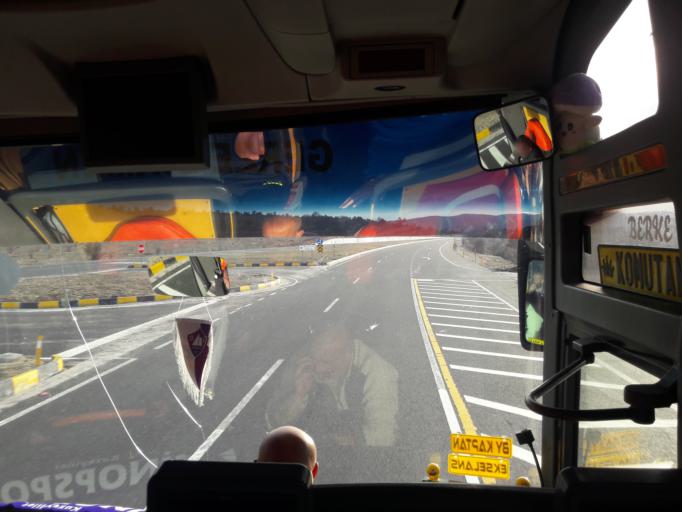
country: TR
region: Cankiri
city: Ilgaz
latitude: 40.8473
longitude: 33.5968
